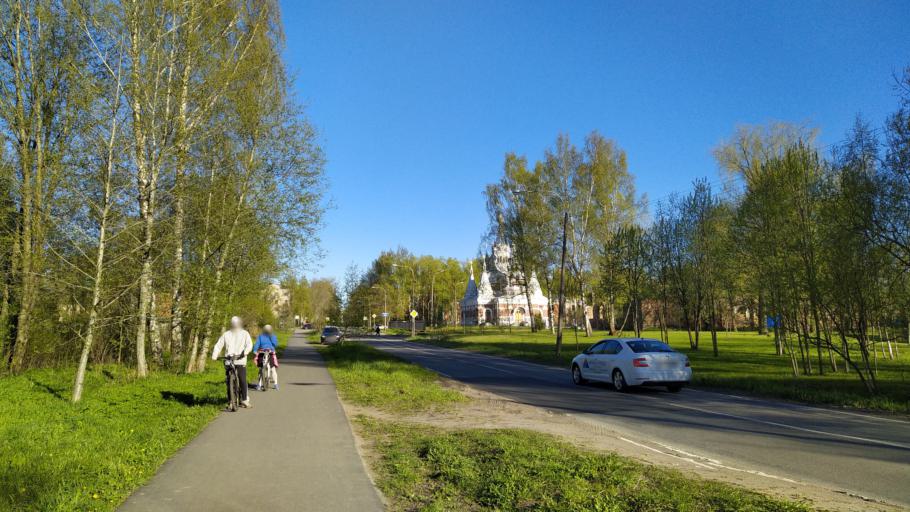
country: RU
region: St.-Petersburg
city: Pavlovsk
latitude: 59.6793
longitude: 30.4481
